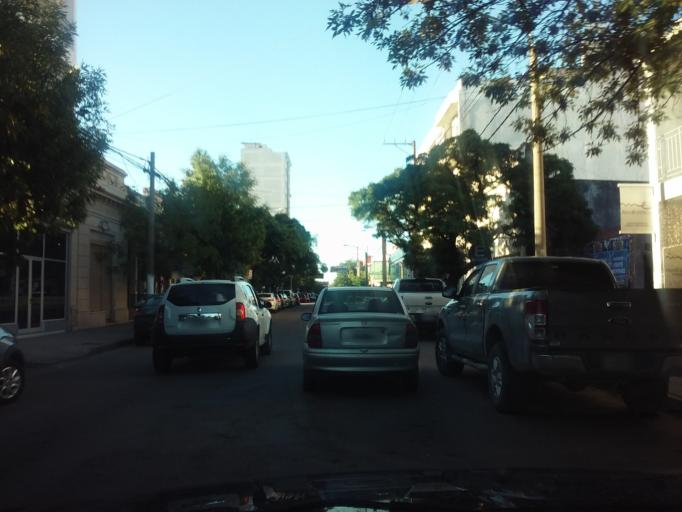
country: AR
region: La Pampa
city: Santa Rosa
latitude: -36.6207
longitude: -64.2938
